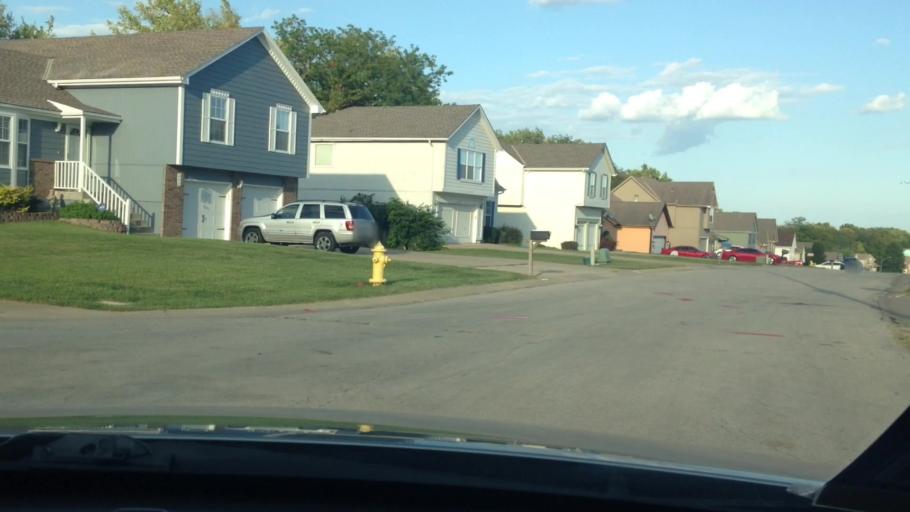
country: US
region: Missouri
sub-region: Jackson County
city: Grandview
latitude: 38.9006
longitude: -94.5146
